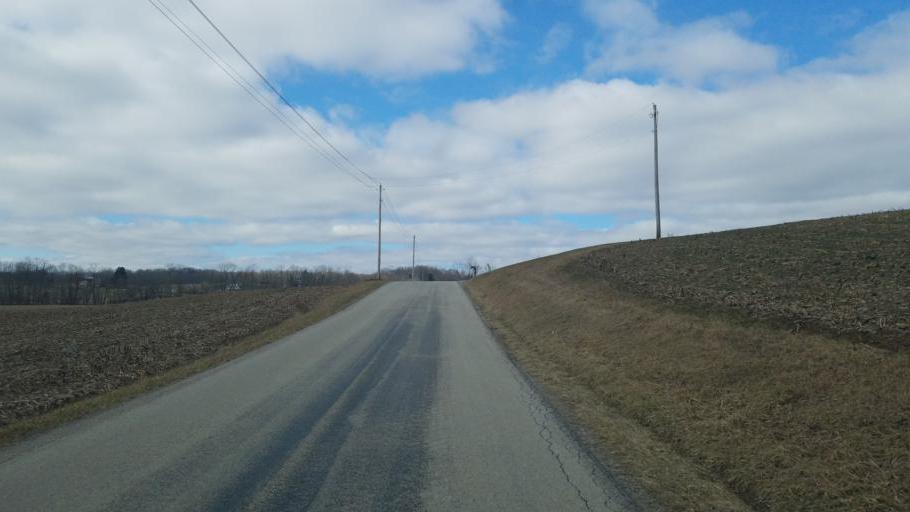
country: US
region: Ohio
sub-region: Sandusky County
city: Bellville
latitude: 40.5562
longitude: -82.5006
